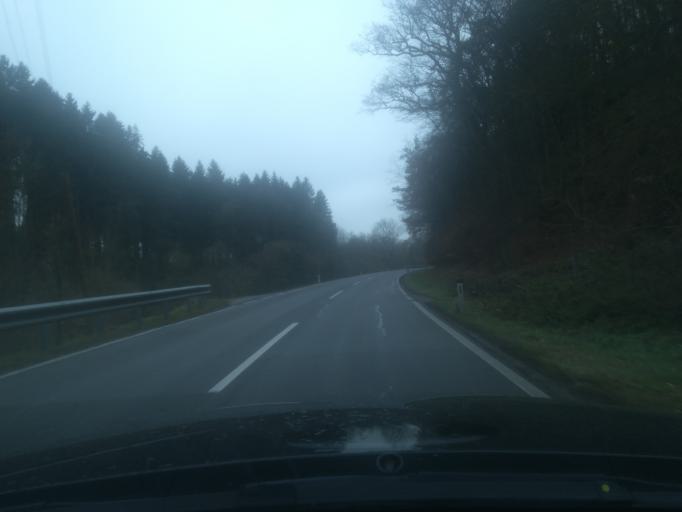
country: AT
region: Upper Austria
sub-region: Politischer Bezirk Perg
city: Perg
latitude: 48.3189
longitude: 14.5705
